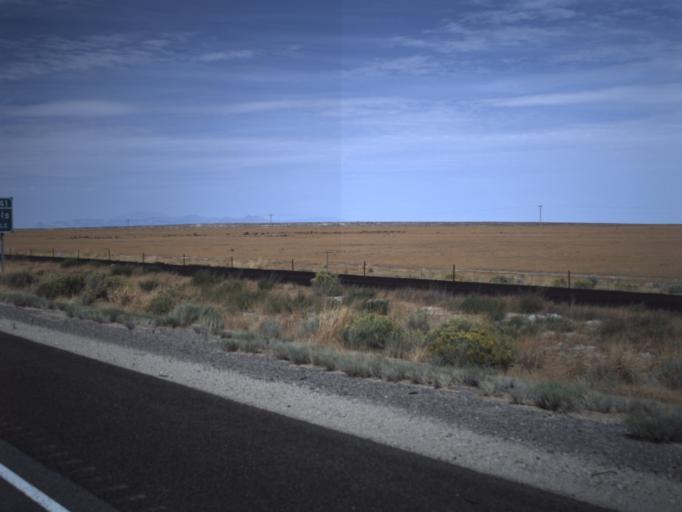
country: US
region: Utah
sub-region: Tooele County
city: Grantsville
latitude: 40.7272
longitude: -113.2422
